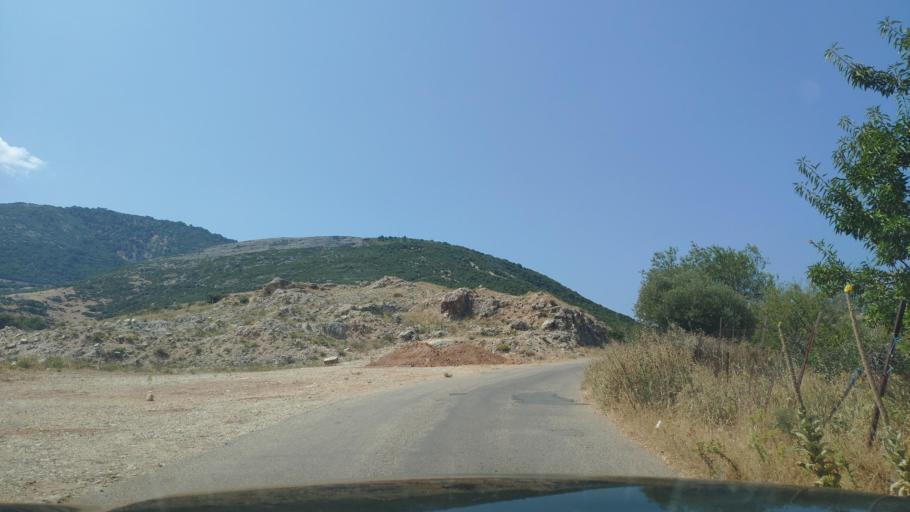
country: GR
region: West Greece
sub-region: Nomos Aitolias kai Akarnanias
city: Monastirakion
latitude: 38.8464
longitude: 20.9442
